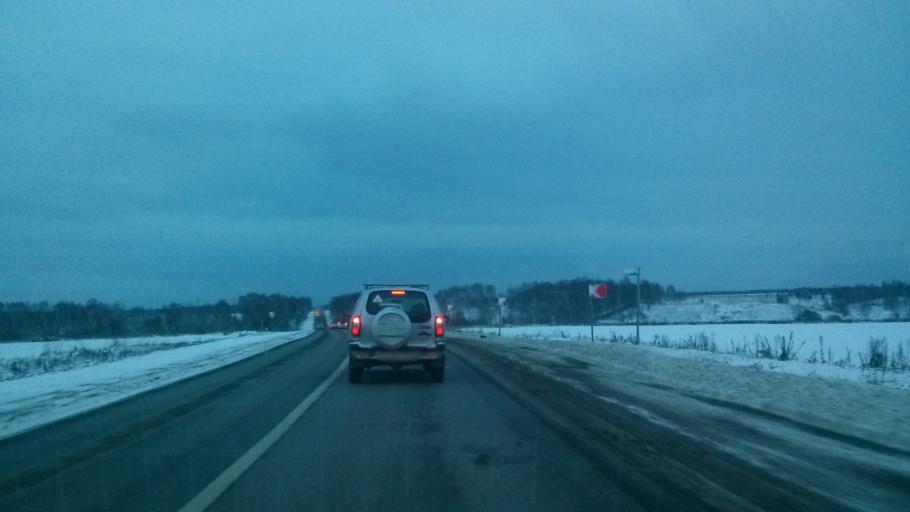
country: RU
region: Nizjnij Novgorod
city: Bogorodsk
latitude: 56.0981
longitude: 43.5831
